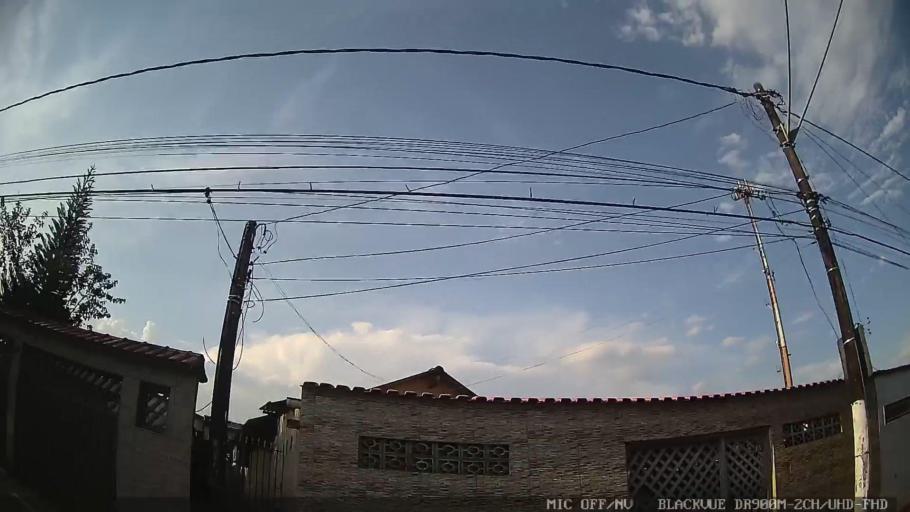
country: BR
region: Sao Paulo
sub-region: Cubatao
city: Cubatao
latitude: -23.9007
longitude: -46.4254
